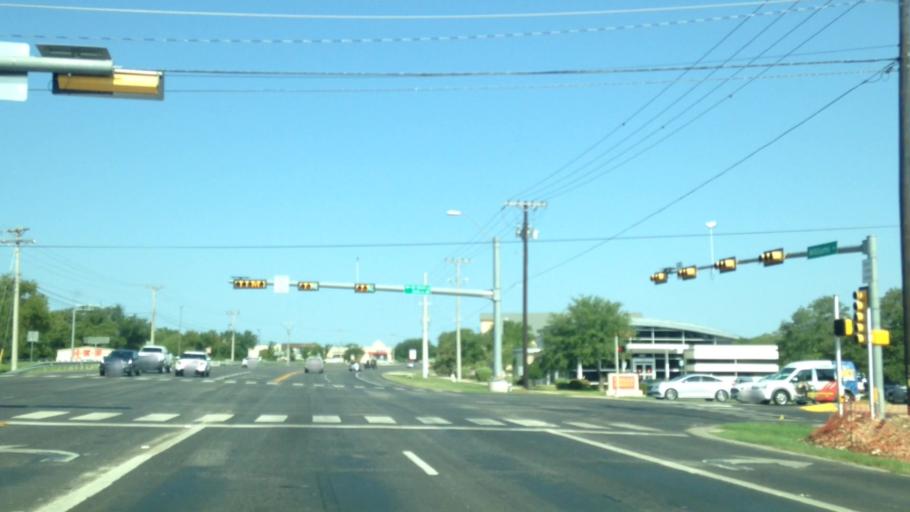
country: US
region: Texas
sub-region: Williamson County
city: Serenada
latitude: 30.6828
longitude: -97.7174
